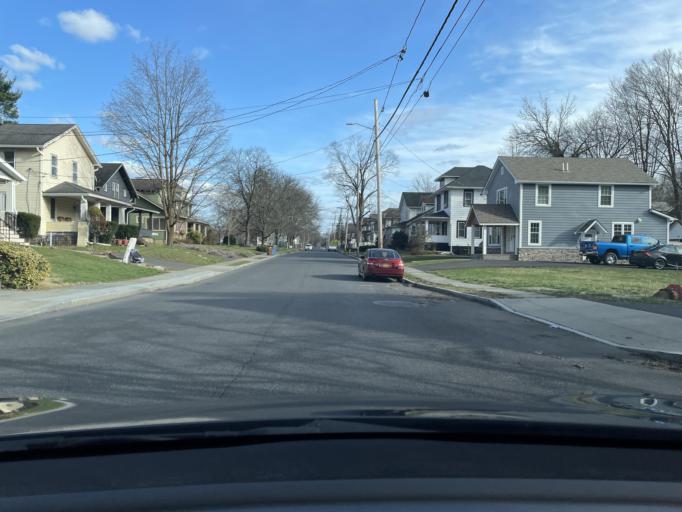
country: US
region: New York
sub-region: Ulster County
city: Kingston
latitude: 41.9268
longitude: -74.0175
